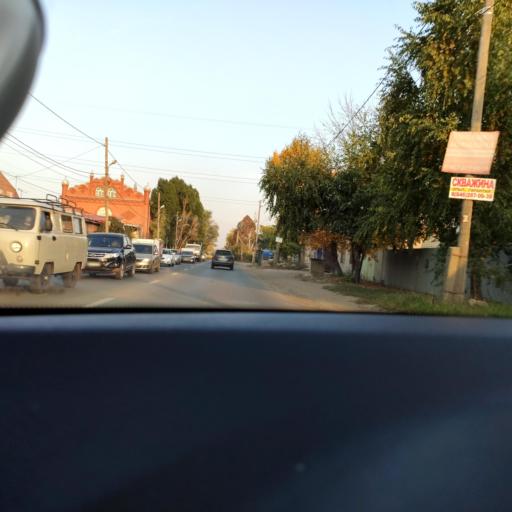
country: RU
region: Samara
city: Petra-Dubrava
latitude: 53.2533
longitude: 50.3165
